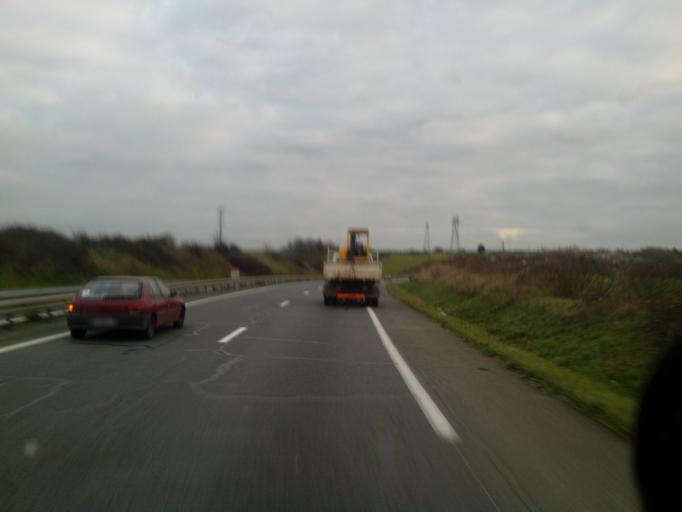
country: FR
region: Poitou-Charentes
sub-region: Departement de la Vienne
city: Chasseneuil-du-Poitou
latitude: 46.6155
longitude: 0.3831
